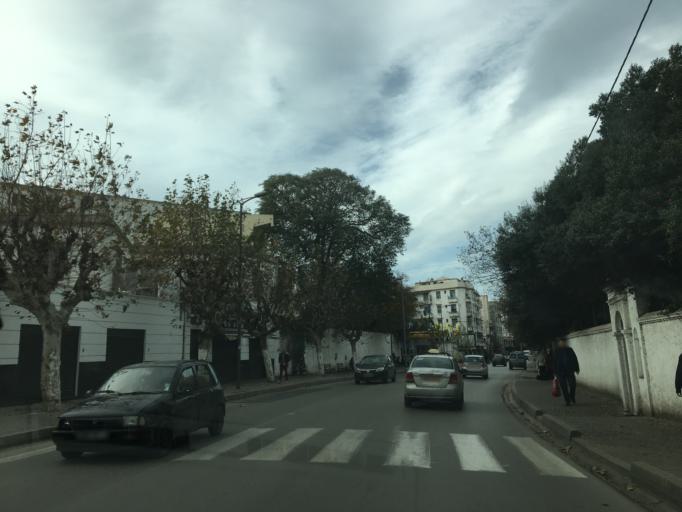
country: DZ
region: Alger
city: Algiers
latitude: 36.7696
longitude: 3.0354
